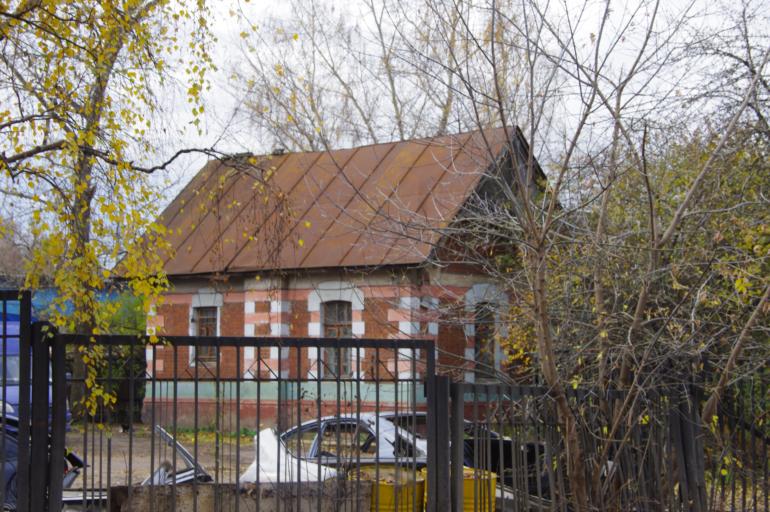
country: RU
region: Moscow
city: Novovladykino
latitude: 55.8481
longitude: 37.5979
